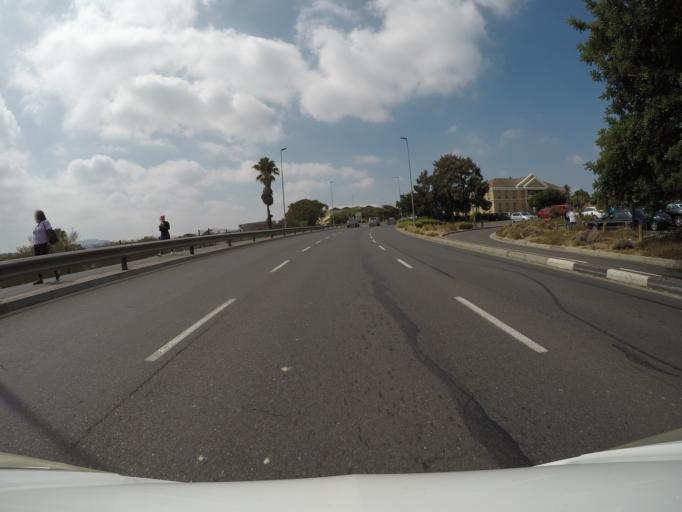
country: ZA
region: Western Cape
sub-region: City of Cape Town
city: Kraaifontein
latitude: -33.8758
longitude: 18.6365
